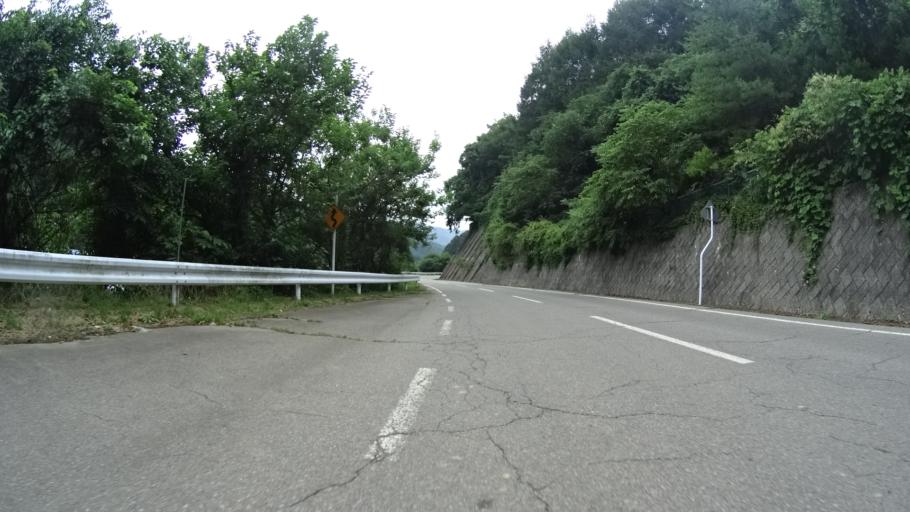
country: JP
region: Nagano
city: Saku
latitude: 36.0709
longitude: 138.5943
